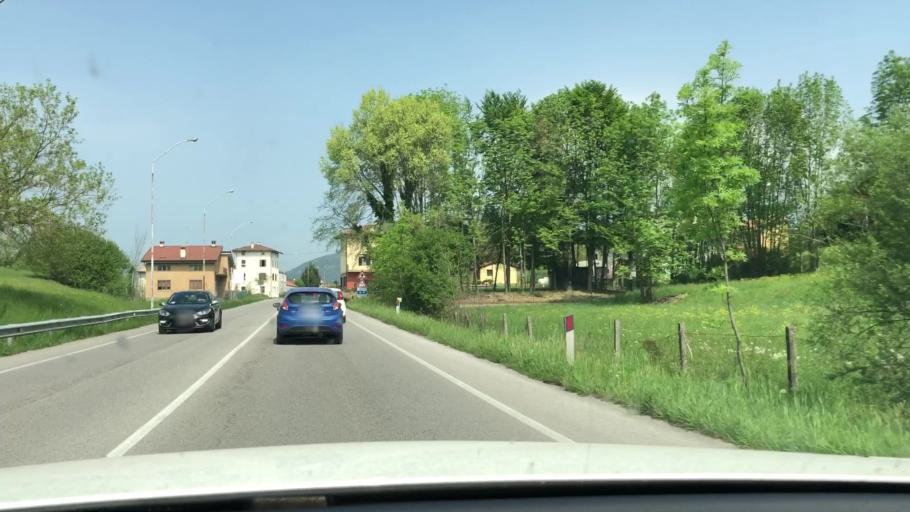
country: IT
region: Friuli Venezia Giulia
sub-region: Provincia di Udine
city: Cassacco
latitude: 46.1950
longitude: 13.1939
